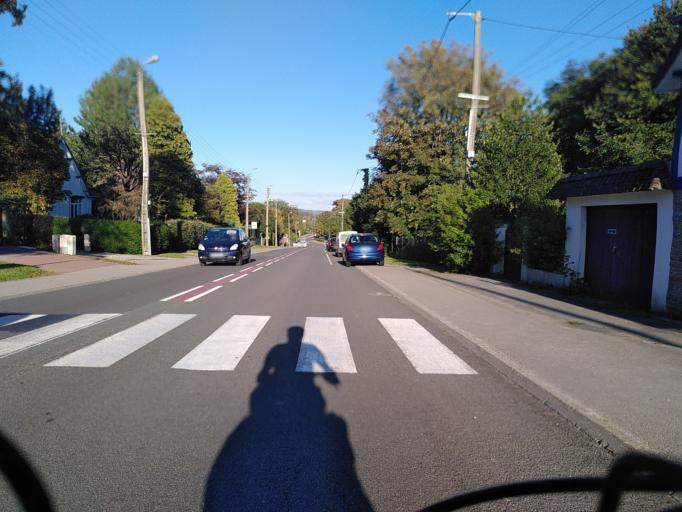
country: FR
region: Nord-Pas-de-Calais
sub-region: Departement du Pas-de-Calais
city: La Capelle-les-Boulogne
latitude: 50.7313
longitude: 1.7110
